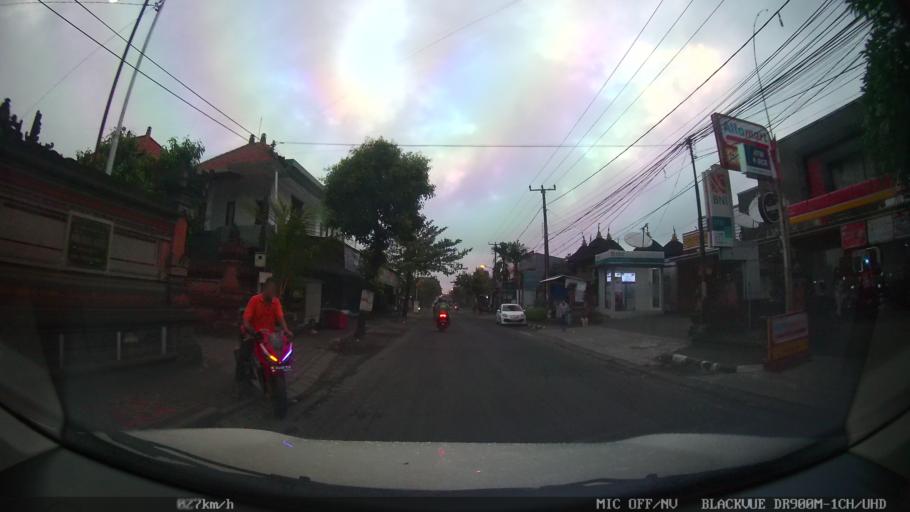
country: ID
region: Bali
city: Banjar Mambalkajanan
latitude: -8.5512
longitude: 115.2197
